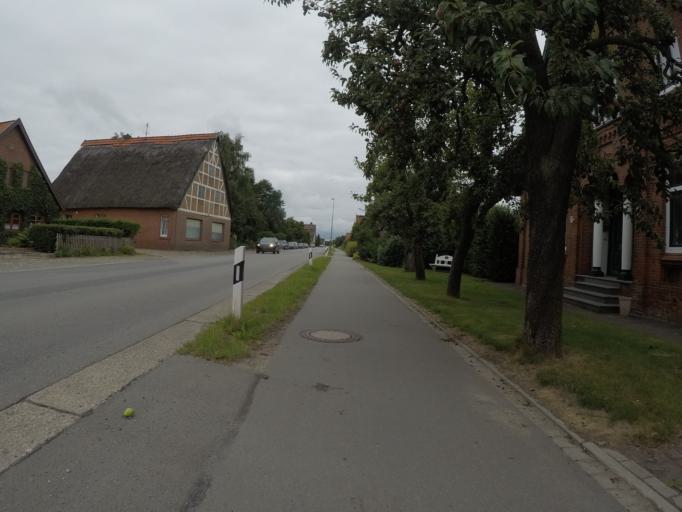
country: DE
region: Lower Saxony
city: Jork
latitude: 53.5365
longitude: 9.6649
